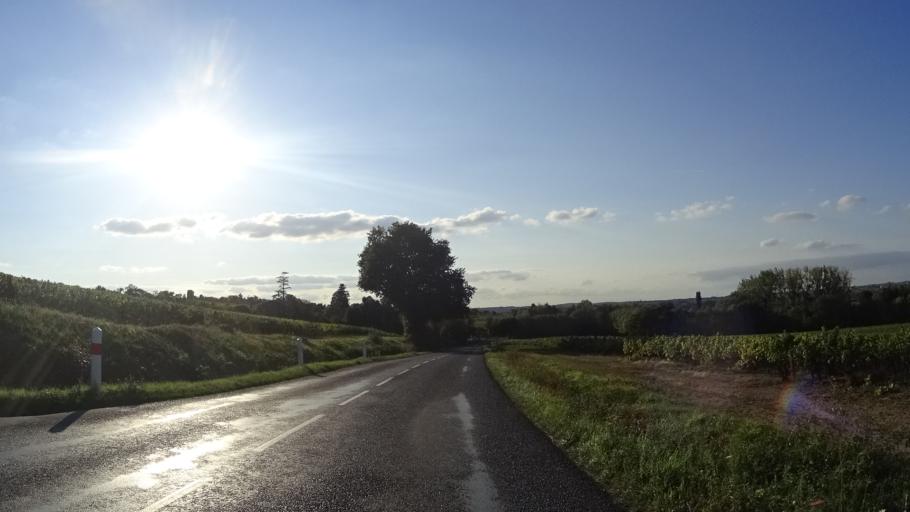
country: FR
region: Pays de la Loire
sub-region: Departement de Maine-et-Loire
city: Lire
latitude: 47.3409
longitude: -1.1398
